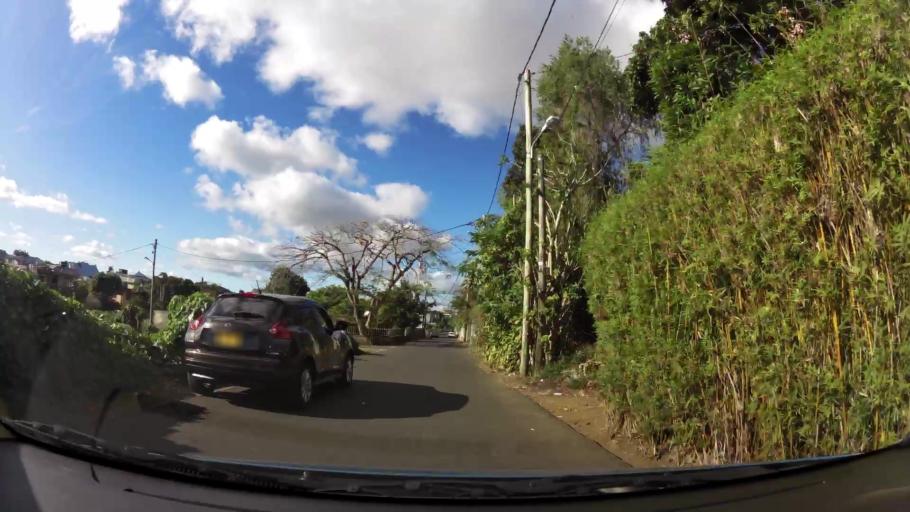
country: MU
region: Plaines Wilhems
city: Vacoas
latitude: -20.2890
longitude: 57.4930
